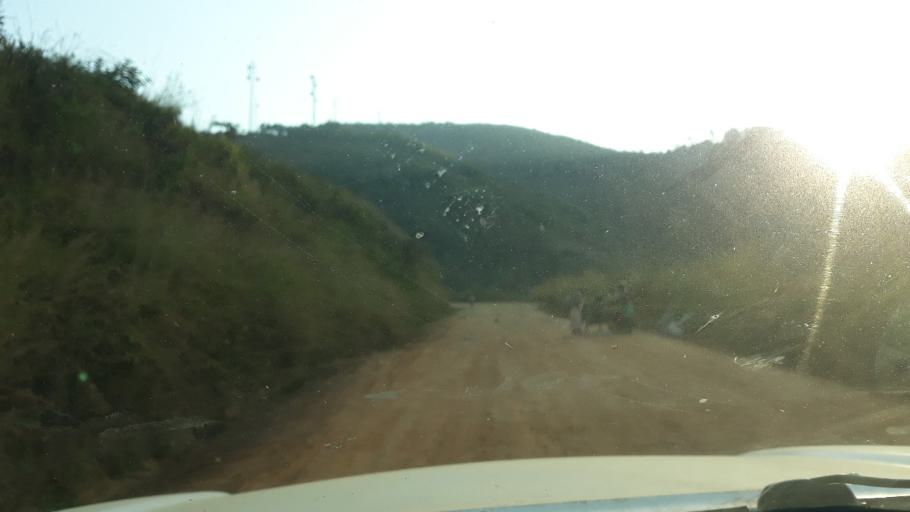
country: RW
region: Western Province
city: Cyangugu
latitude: -2.7027
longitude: 28.9121
